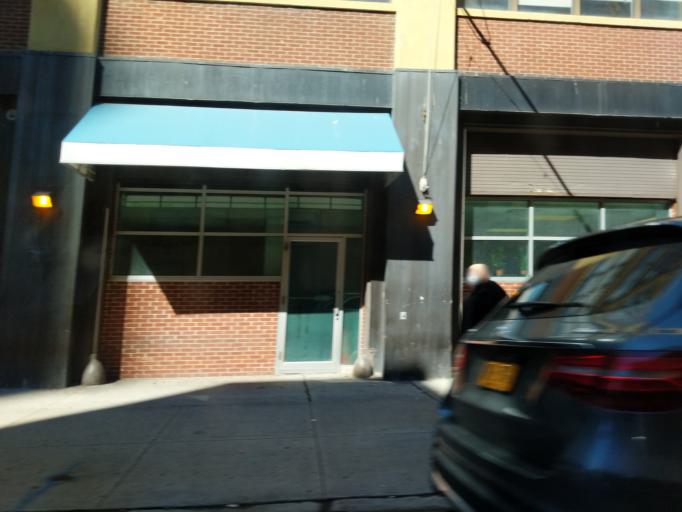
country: US
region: New York
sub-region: New York County
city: Manhattan
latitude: 40.7826
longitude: -73.9471
